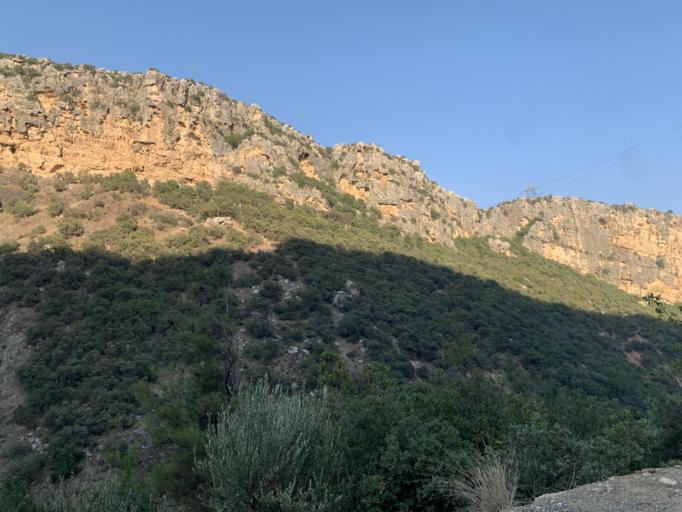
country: TR
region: Mersin
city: Mercin
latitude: 36.8833
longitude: 34.5492
